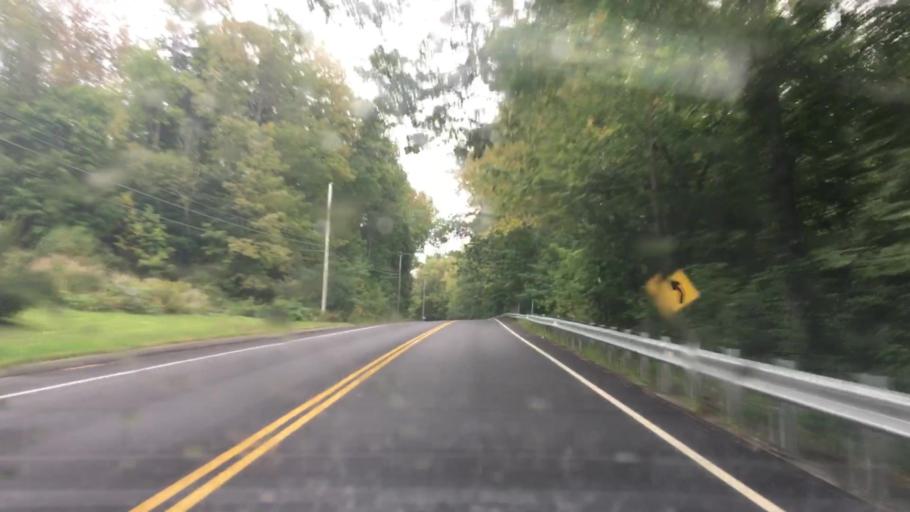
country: US
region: Maine
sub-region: Penobscot County
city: Orrington
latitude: 44.6808
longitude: -68.8082
